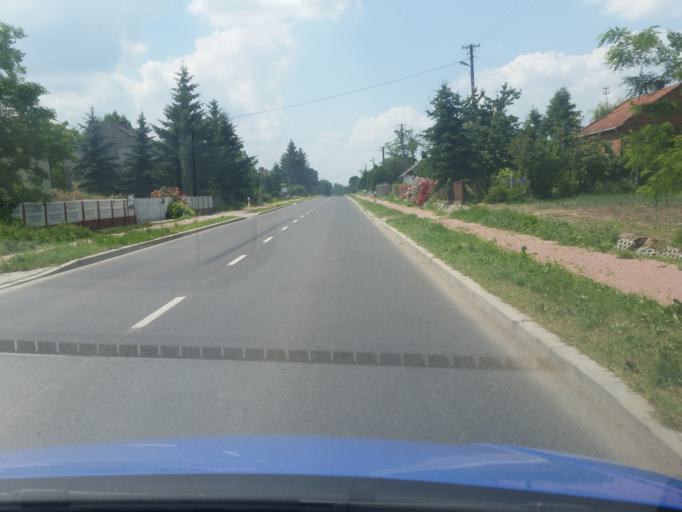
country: PL
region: Swietokrzyskie
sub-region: Powiat pinczowski
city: Zlota
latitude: 50.3381
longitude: 20.6220
